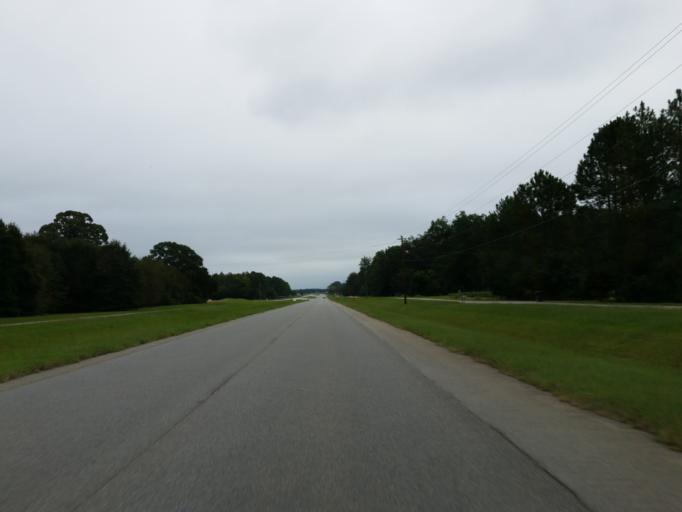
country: US
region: Georgia
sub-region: Houston County
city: Perry
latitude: 32.4302
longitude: -83.7479
